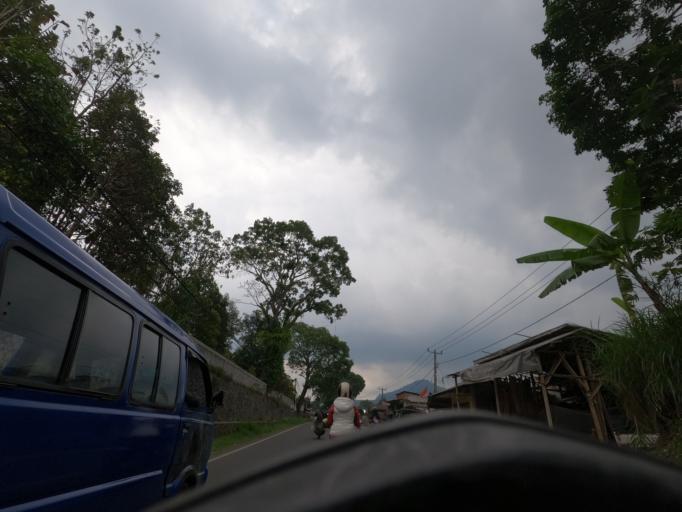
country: ID
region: West Java
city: Sukabumi
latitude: -6.7834
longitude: 107.0635
